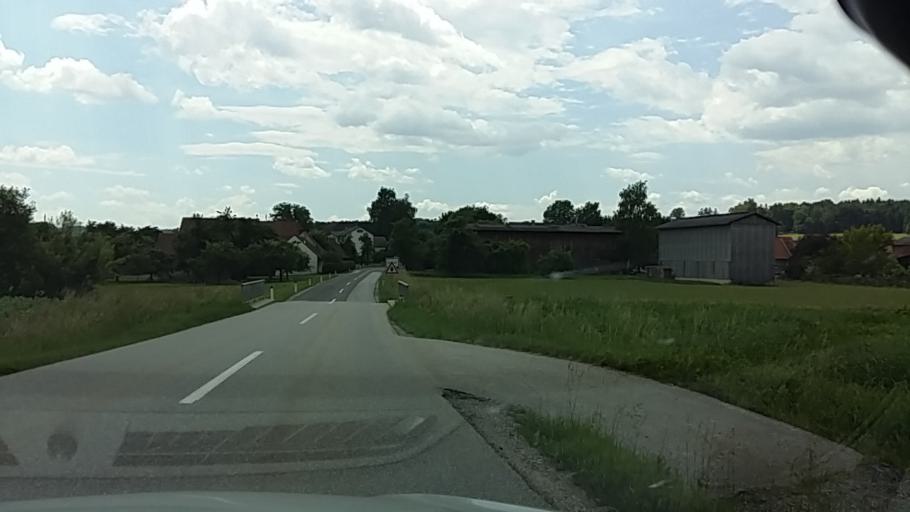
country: AT
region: Styria
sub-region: Politischer Bezirk Hartberg-Fuerstenfeld
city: Hainersdorf
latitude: 47.0956
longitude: 15.9594
